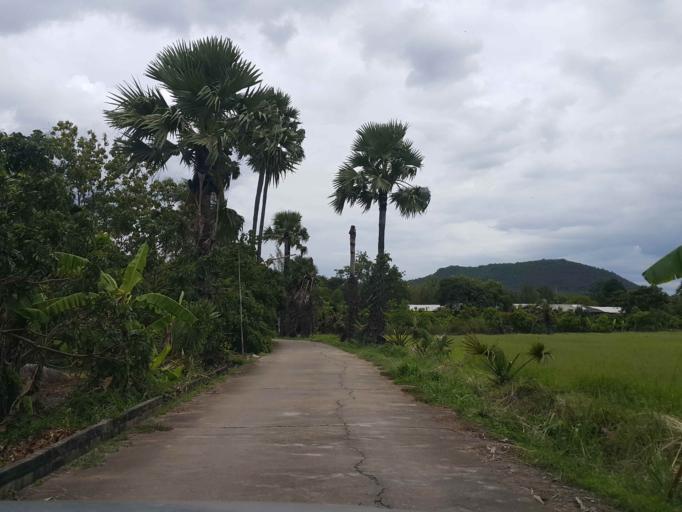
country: TH
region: Lamphun
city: Pa Sang
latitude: 18.4622
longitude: 98.9122
